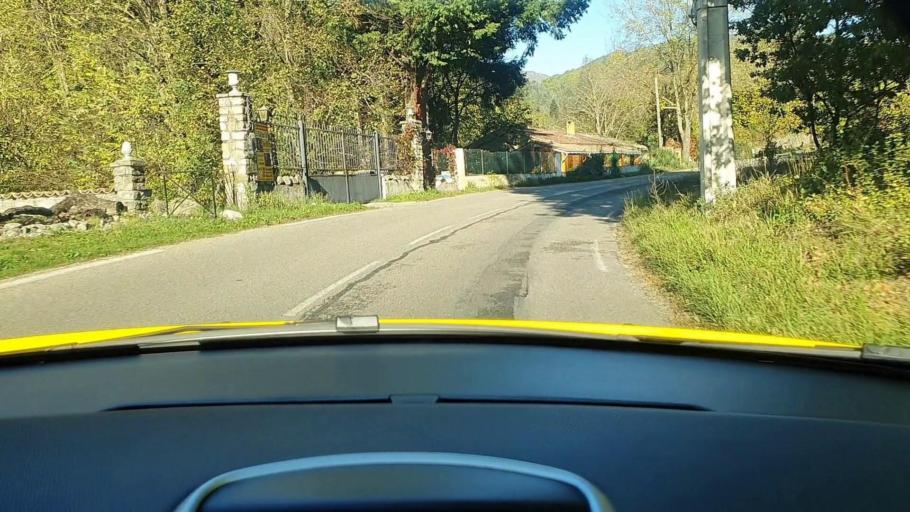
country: FR
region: Languedoc-Roussillon
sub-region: Departement du Gard
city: Le Vigan
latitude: 43.9862
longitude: 3.5822
